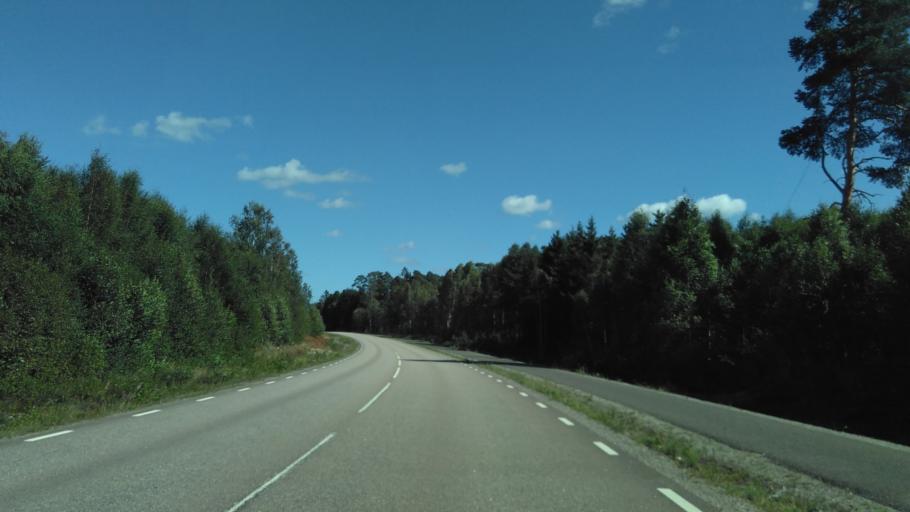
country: SE
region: Vaestra Goetaland
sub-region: Skara Kommun
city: Axvall
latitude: 58.3988
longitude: 13.5431
